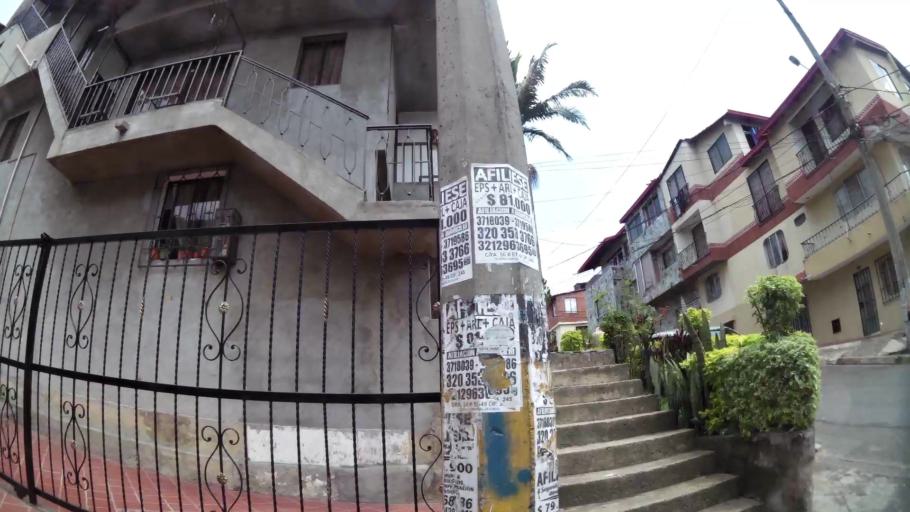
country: CO
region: Antioquia
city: Itagui
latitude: 6.1821
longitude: -75.6054
